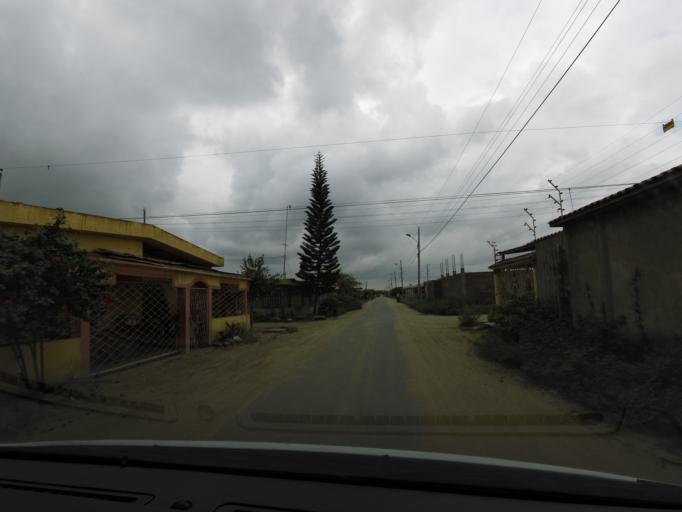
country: EC
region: El Oro
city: Huaquillas
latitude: -3.4842
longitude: -80.2075
